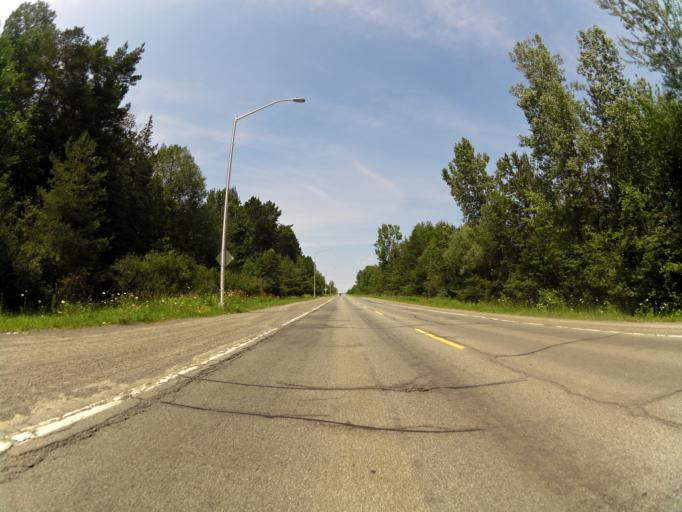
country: CA
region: Ontario
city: Ottawa
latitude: 45.3565
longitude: -75.6145
